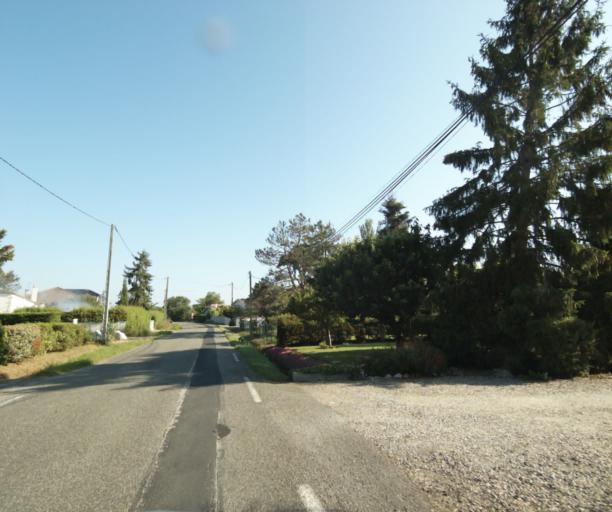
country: FR
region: Midi-Pyrenees
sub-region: Departement du Tarn-et-Garonne
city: Saint-Etienne-de-Tulmont
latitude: 44.0402
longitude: 1.4220
